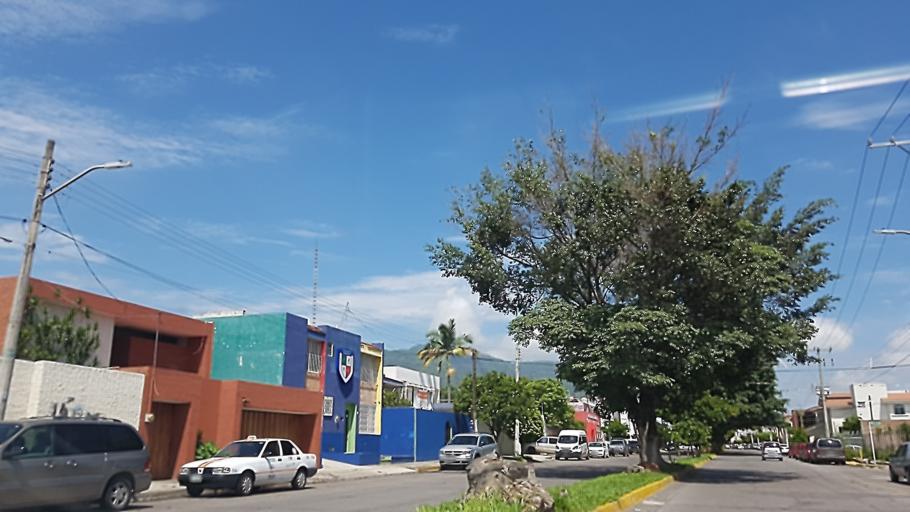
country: MX
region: Nayarit
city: Tepic
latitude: 21.4852
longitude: -104.8828
